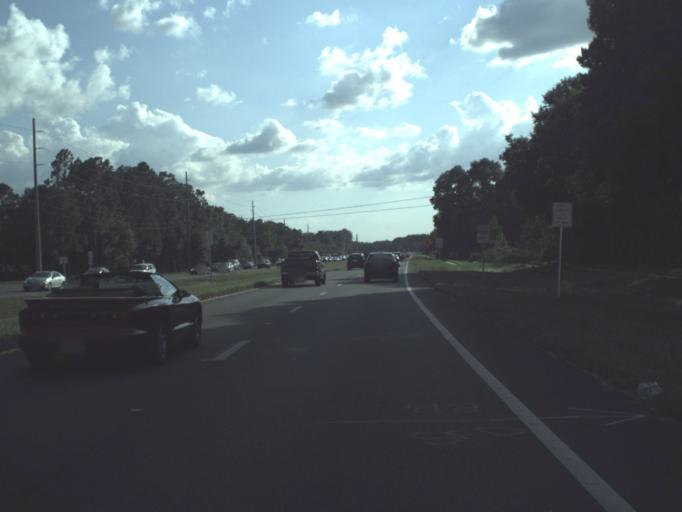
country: US
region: Florida
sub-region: Hillsborough County
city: Lutz
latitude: 28.1574
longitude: -82.4842
